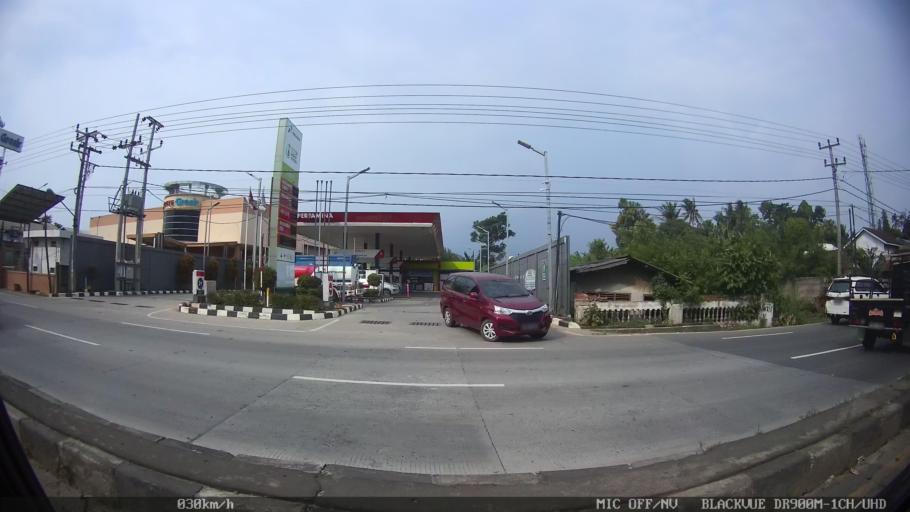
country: ID
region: Lampung
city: Kedaton
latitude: -5.3545
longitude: 105.2213
